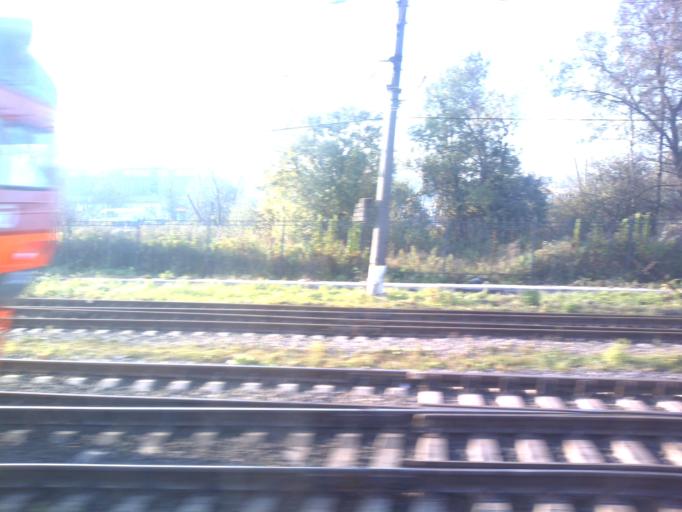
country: RU
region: St.-Petersburg
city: Krasnogvargeisky
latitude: 59.9816
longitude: 30.5100
